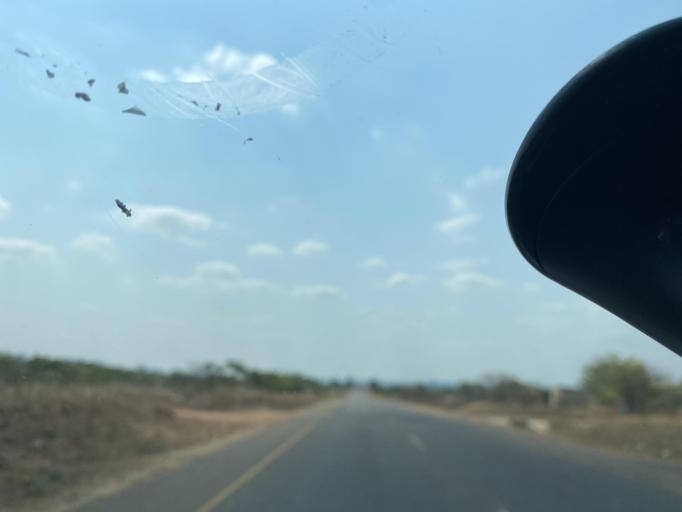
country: ZM
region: Lusaka
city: Chongwe
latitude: -15.5890
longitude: 28.7116
